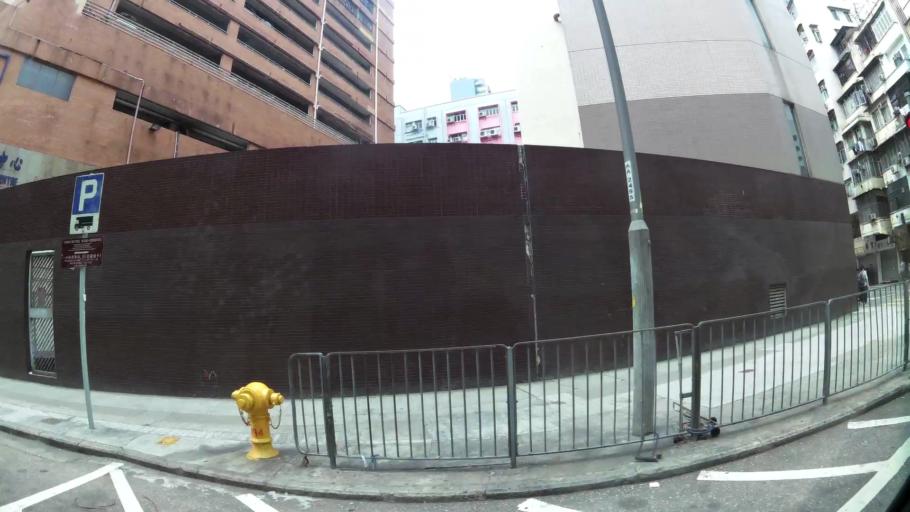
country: HK
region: Sham Shui Po
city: Sham Shui Po
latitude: 22.3394
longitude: 114.1519
